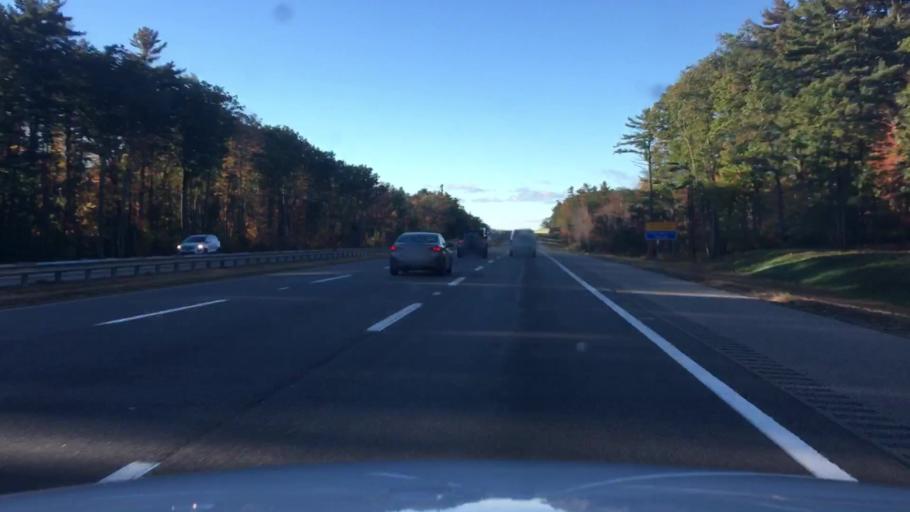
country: US
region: Maine
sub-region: York County
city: Wells Beach Station
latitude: 43.3642
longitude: -70.5855
